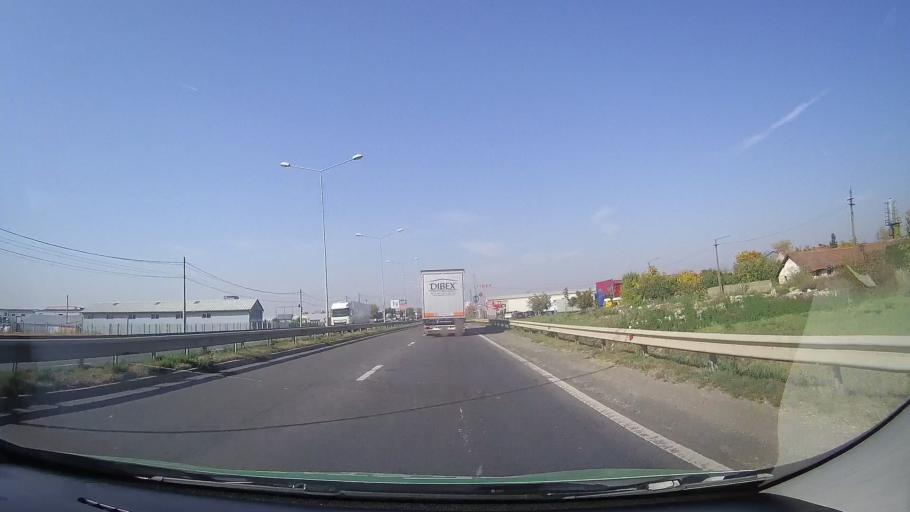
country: RO
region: Bihor
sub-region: Comuna Santandrei
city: Santandrei
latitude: 47.0486
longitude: 21.8910
